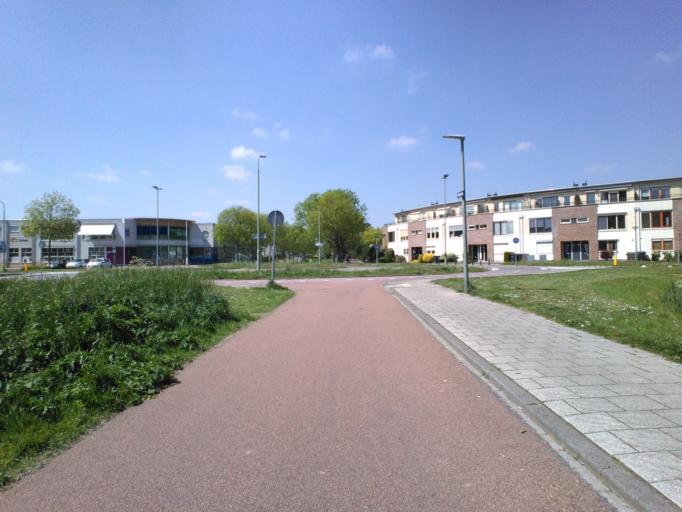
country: NL
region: South Holland
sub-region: Gemeente Papendrecht
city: Papendrecht
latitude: 51.8065
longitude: 4.7151
